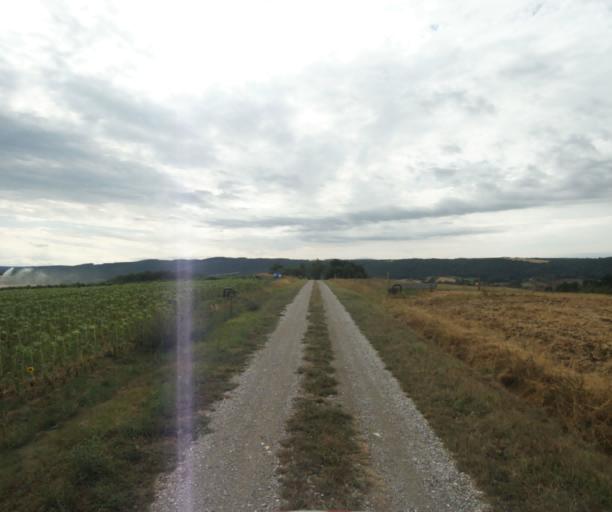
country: FR
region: Midi-Pyrenees
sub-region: Departement de la Haute-Garonne
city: Revel
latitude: 43.4267
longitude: 1.9680
